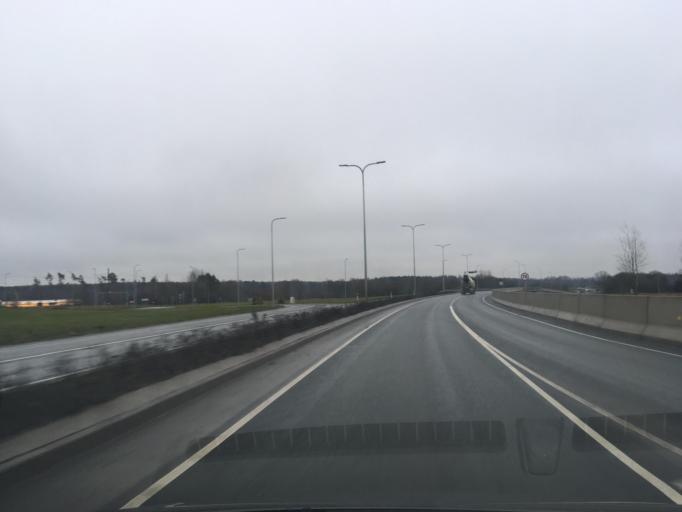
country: EE
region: Tartu
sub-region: Tartu linn
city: Tartu
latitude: 58.3721
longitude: 26.7817
